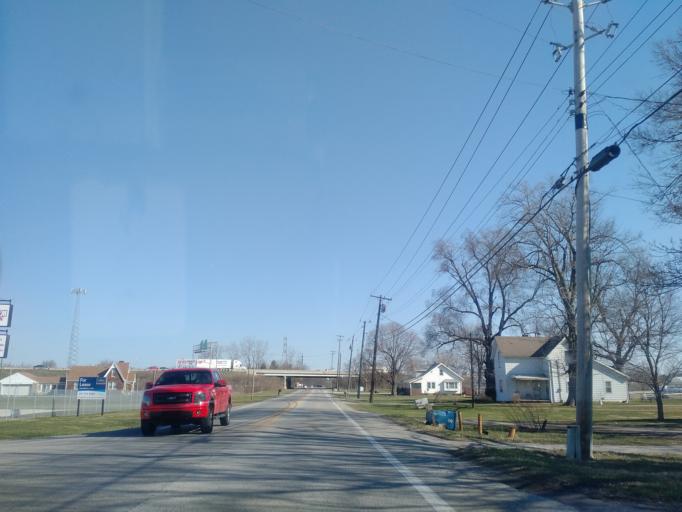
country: US
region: Indiana
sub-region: Marion County
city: Southport
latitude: 39.6975
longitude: -86.1726
